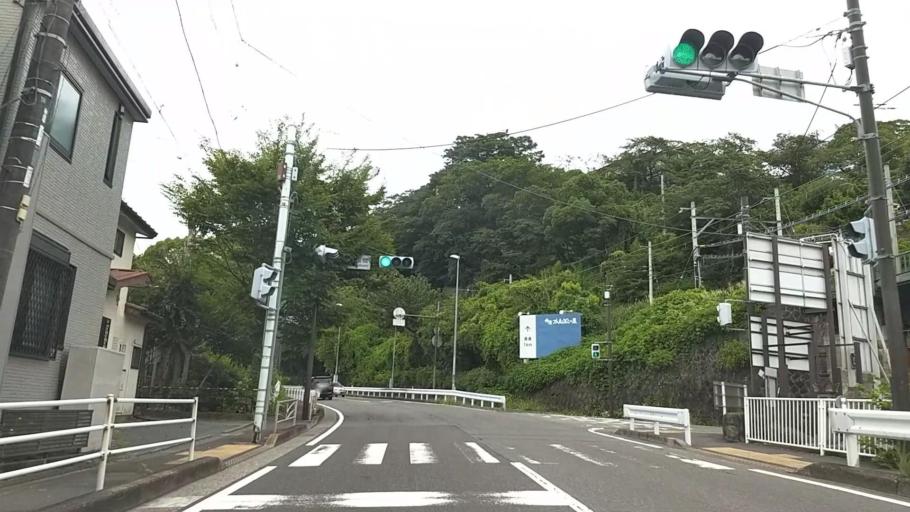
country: JP
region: Kanagawa
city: Odawara
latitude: 35.2467
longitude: 139.1406
